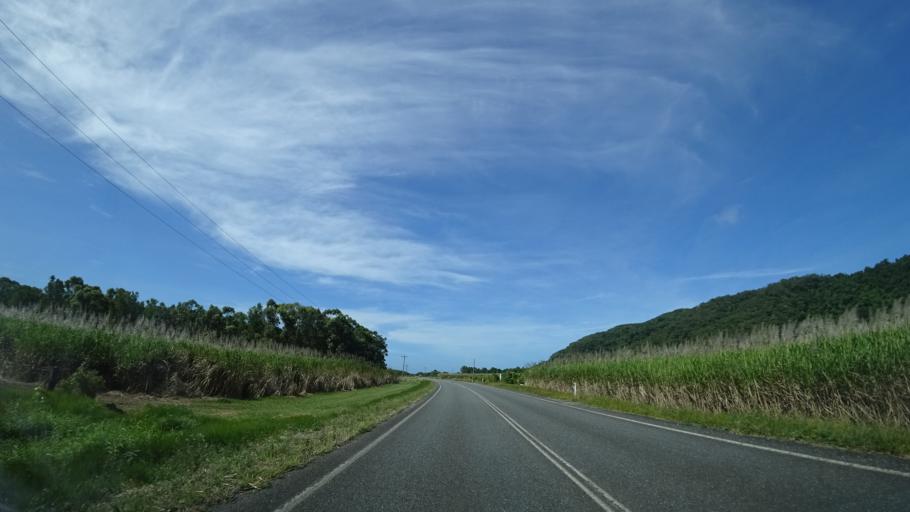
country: AU
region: Queensland
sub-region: Cairns
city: Port Douglas
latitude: -16.3112
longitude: 145.3962
